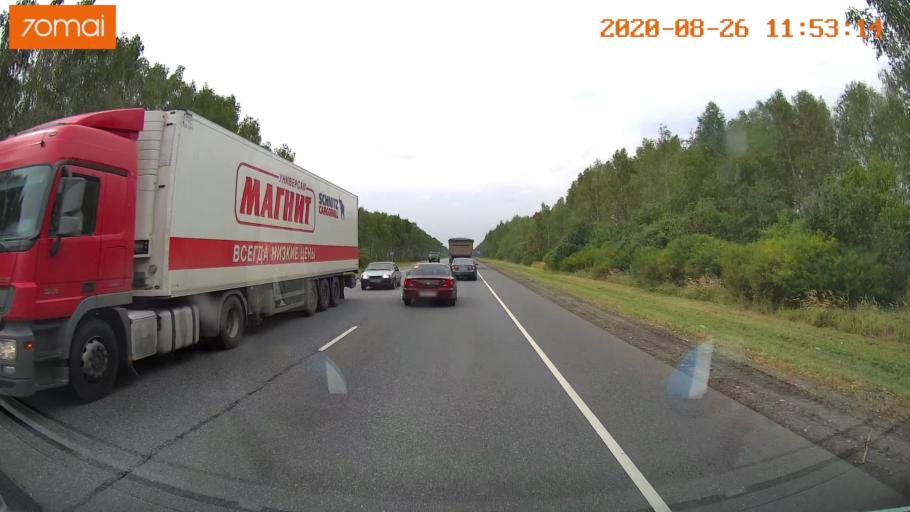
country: RU
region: Rjazan
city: Kiritsy
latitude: 54.2916
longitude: 40.4355
